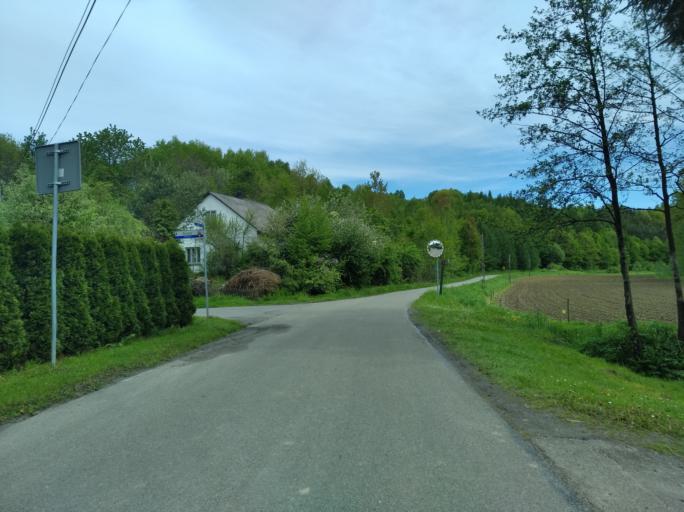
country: PL
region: Subcarpathian Voivodeship
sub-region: Powiat strzyzowski
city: Strzyzow
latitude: 49.9256
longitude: 21.7538
